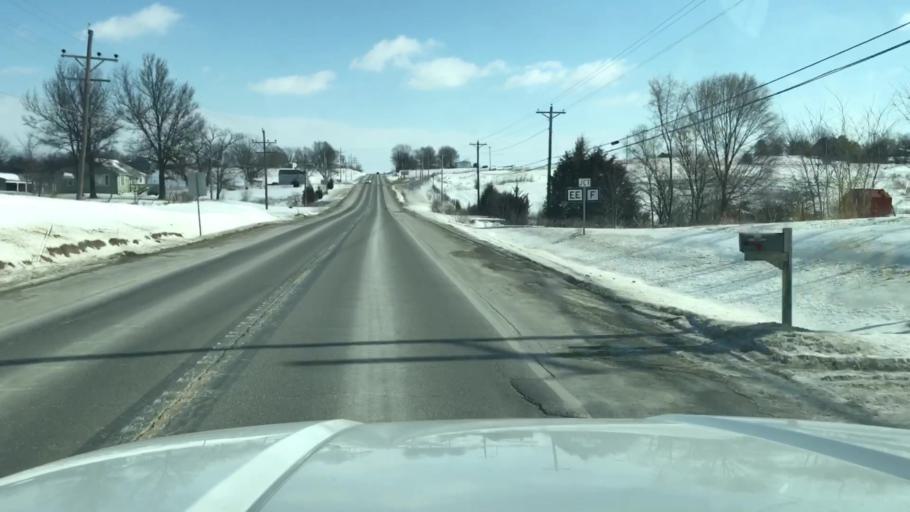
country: US
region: Missouri
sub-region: Nodaway County
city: Maryville
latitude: 40.3446
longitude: -94.8017
